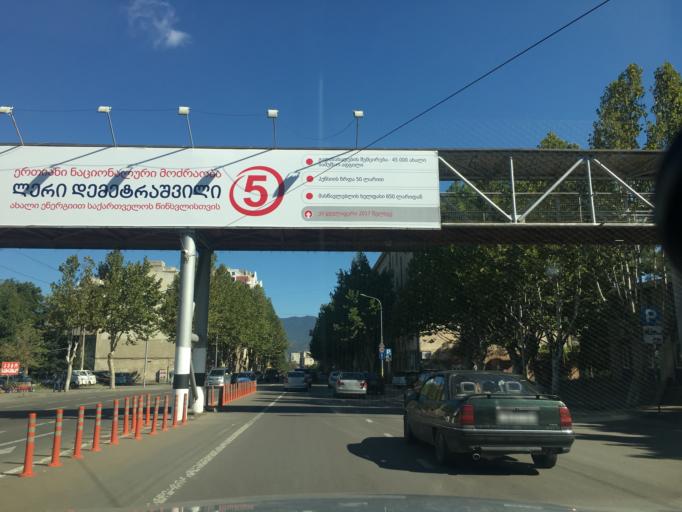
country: GE
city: Zahesi
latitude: 41.7698
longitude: 44.7926
